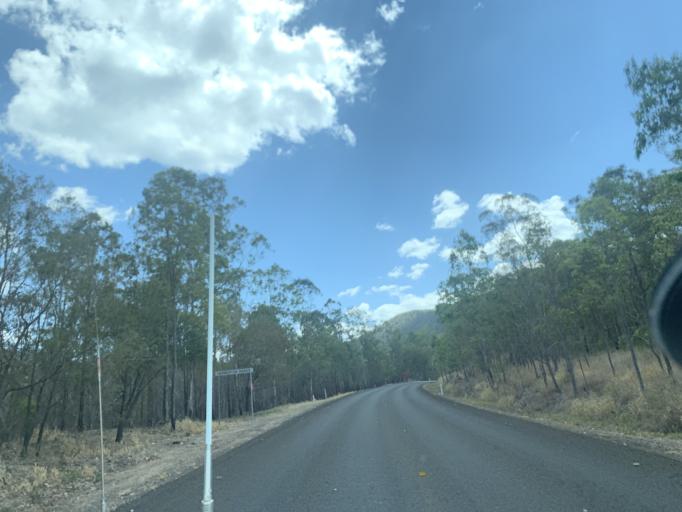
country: AU
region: Queensland
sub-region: Tablelands
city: Atherton
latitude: -17.3303
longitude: 145.4358
